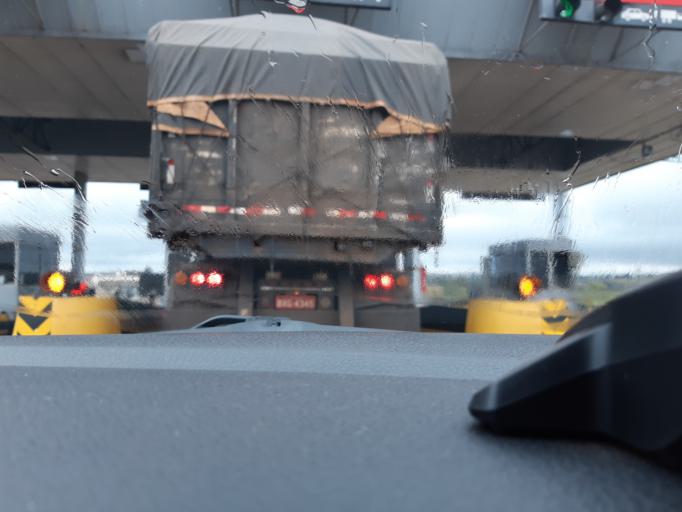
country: BR
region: Sao Paulo
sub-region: Ourinhos
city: Ourinhos
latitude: -23.0041
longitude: -49.9099
